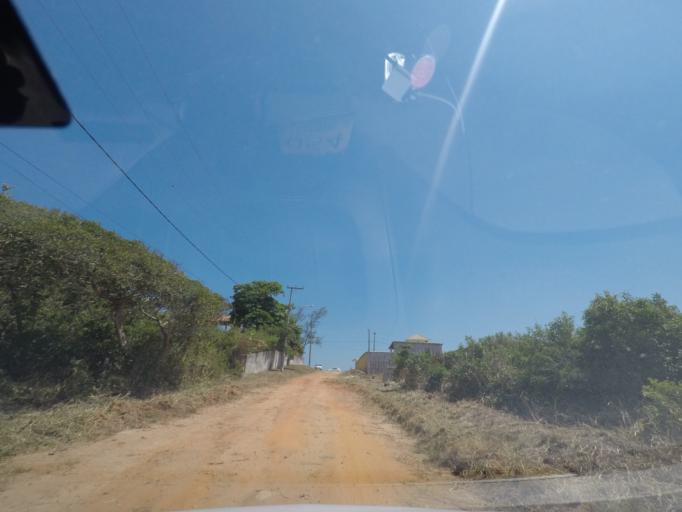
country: BR
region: Rio de Janeiro
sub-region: Marica
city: Marica
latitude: -22.9728
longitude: -42.9289
